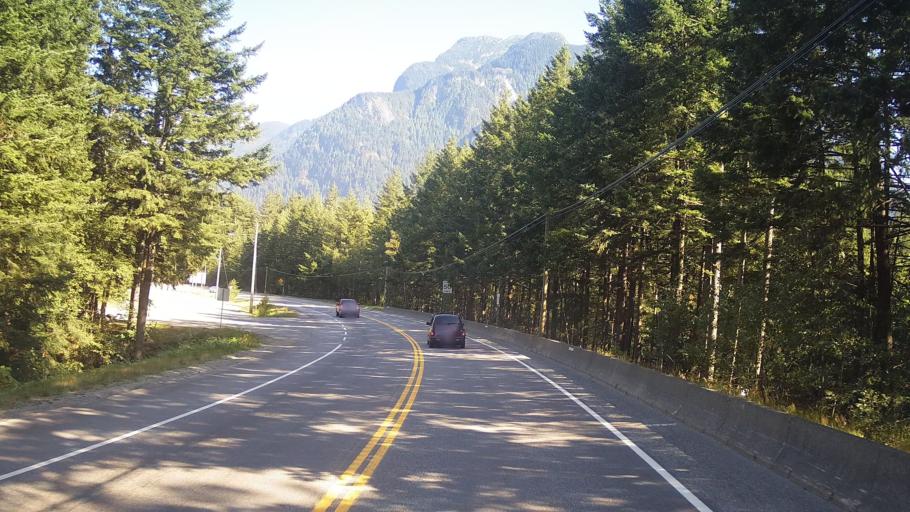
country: CA
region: British Columbia
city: Hope
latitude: 49.3873
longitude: -121.4606
